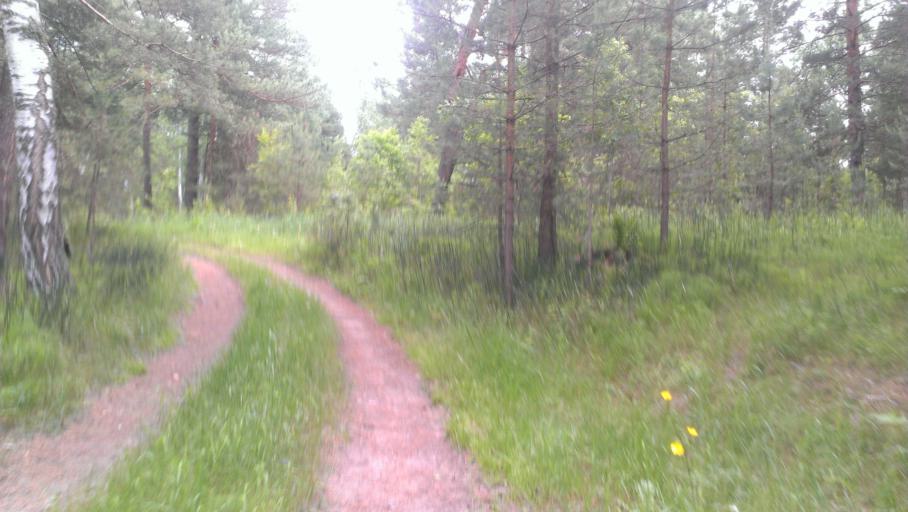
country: RU
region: Altai Krai
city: Sannikovo
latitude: 53.3493
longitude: 84.0343
